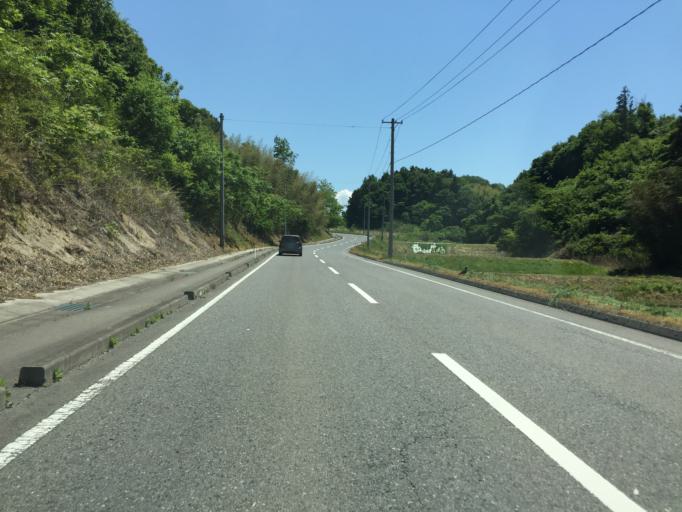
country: JP
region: Fukushima
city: Motomiya
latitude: 37.5228
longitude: 140.4524
